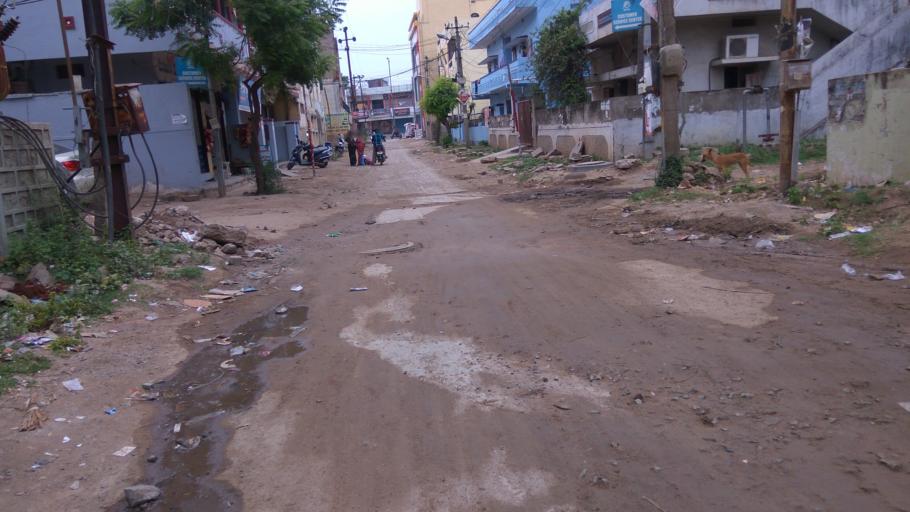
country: IN
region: Telangana
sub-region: Hyderabad
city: Malkajgiri
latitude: 17.4463
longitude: 78.5346
